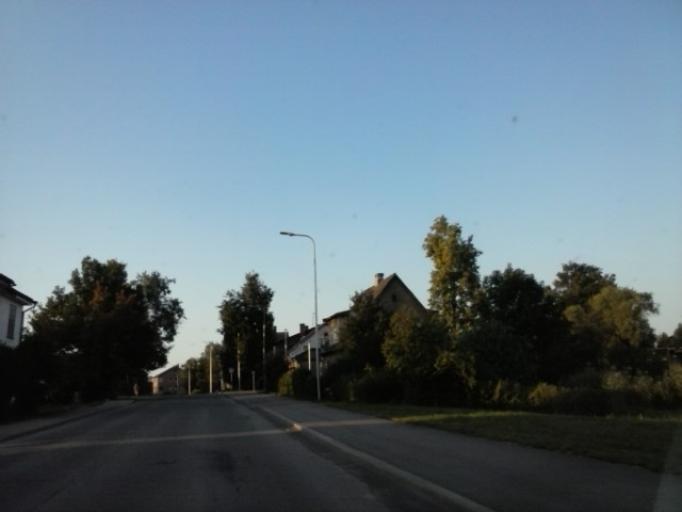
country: EE
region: Vorumaa
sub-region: Voru linn
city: Voru
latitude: 57.8510
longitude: 27.0012
